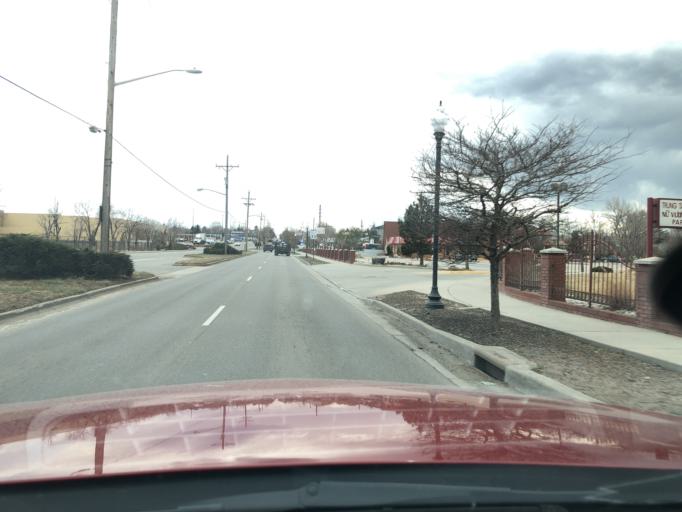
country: US
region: Colorado
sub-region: Jefferson County
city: Wheat Ridge
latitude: 39.7817
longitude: -105.0627
